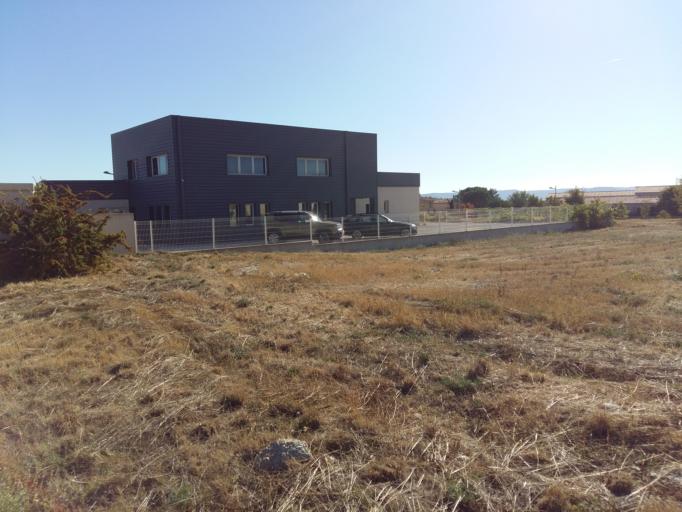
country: FR
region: Provence-Alpes-Cote d'Azur
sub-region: Departement du Vaucluse
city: Pertuis
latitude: 43.7234
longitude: 5.5395
